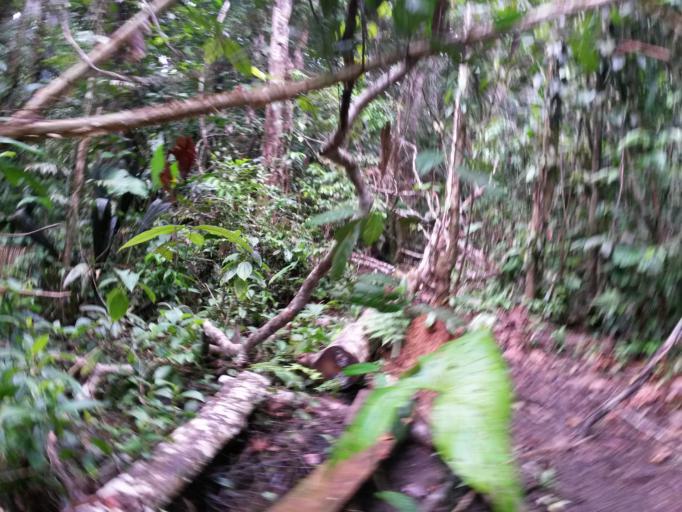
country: CO
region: Putumayo
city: Puerto Guzman
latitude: 1.0101
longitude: -76.3473
